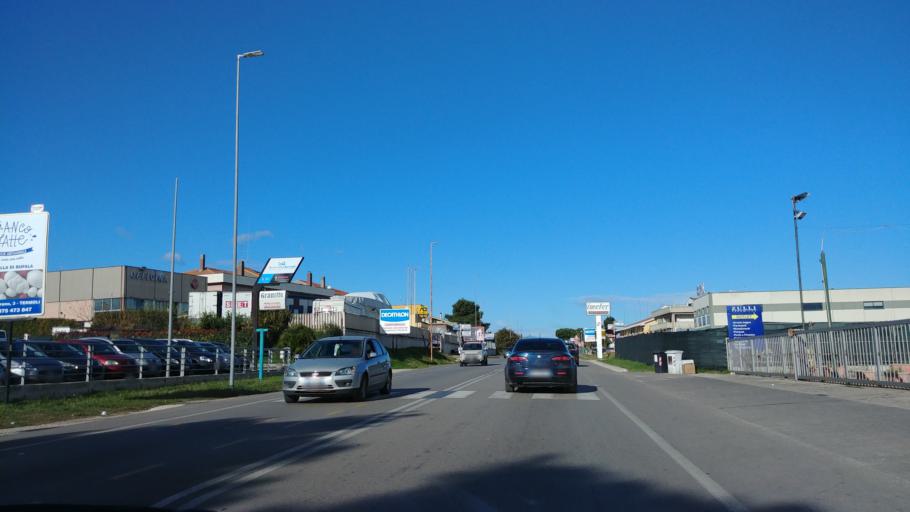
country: IT
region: Molise
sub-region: Provincia di Campobasso
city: Termoli
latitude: 41.9834
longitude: 15.0053
